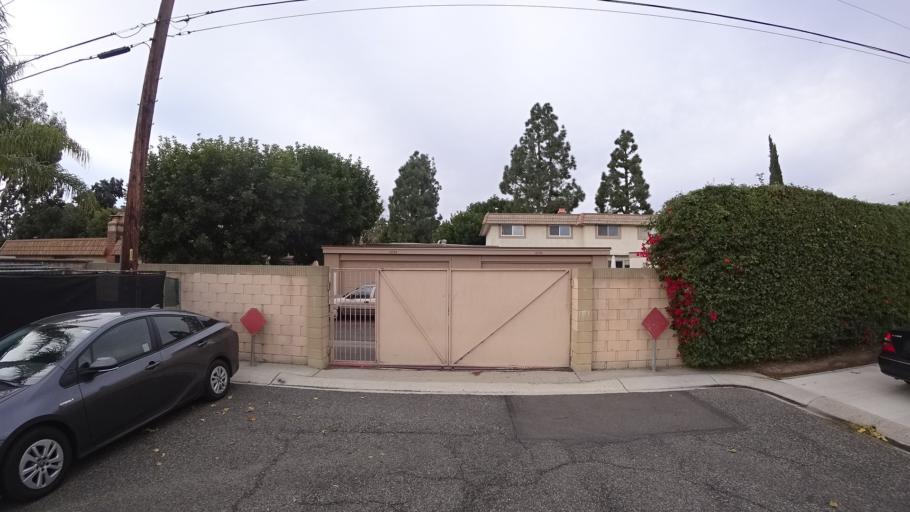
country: US
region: California
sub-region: Orange County
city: Garden Grove
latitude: 33.7776
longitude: -117.9278
